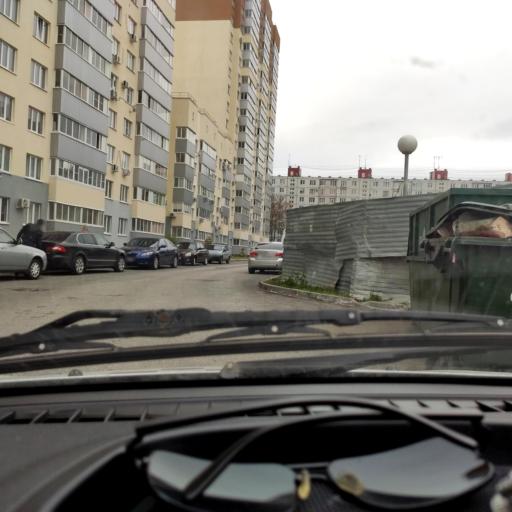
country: RU
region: Samara
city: Tol'yatti
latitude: 53.5082
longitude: 49.4245
